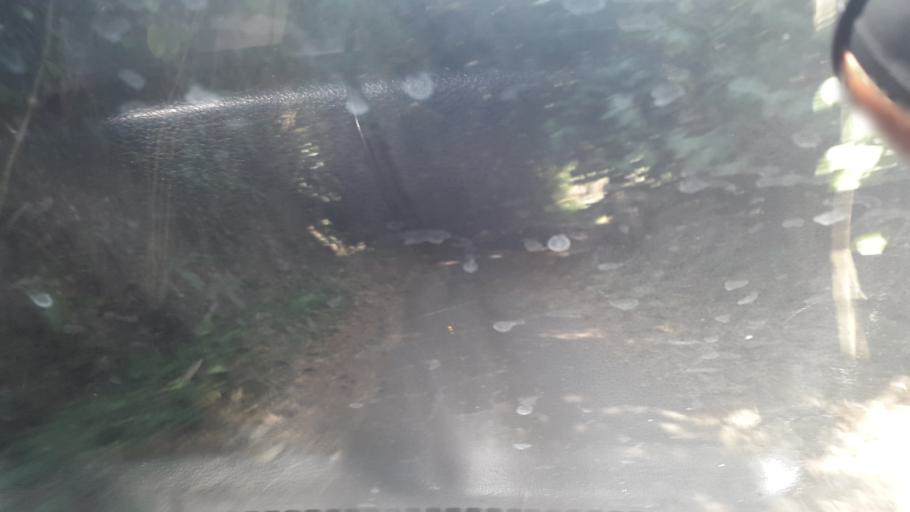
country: ID
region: West Java
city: Pasirreungit
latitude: -7.0103
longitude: 107.0181
